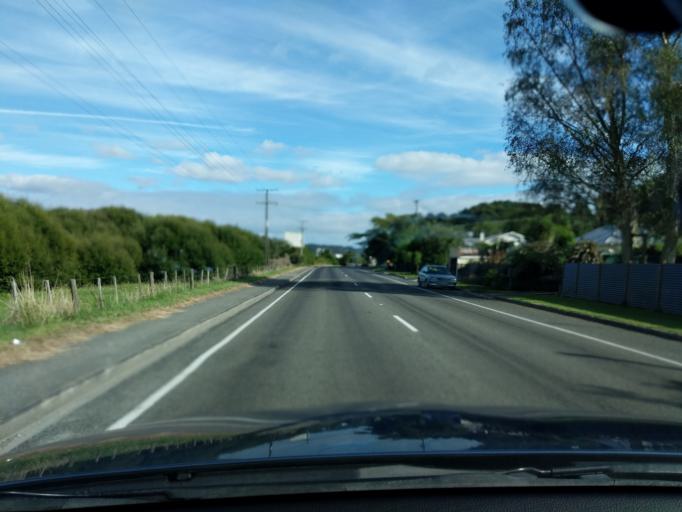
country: NZ
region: Tasman
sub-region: Tasman District
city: Takaka
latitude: -40.8571
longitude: 172.8189
